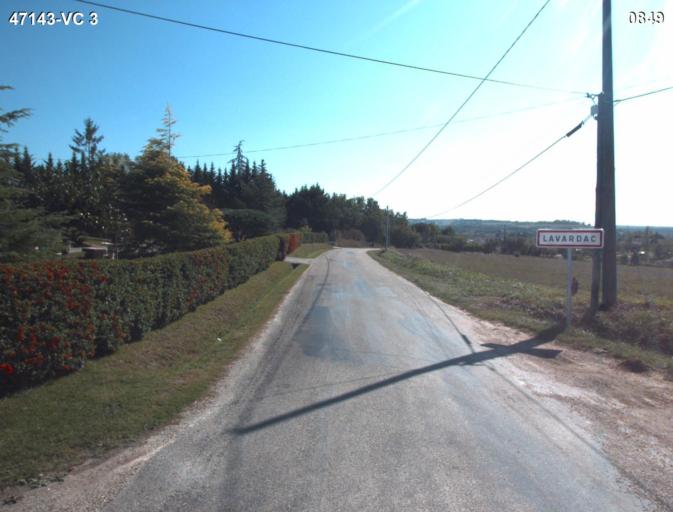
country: FR
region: Aquitaine
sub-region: Departement du Lot-et-Garonne
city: Lavardac
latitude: 44.1911
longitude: 0.2948
